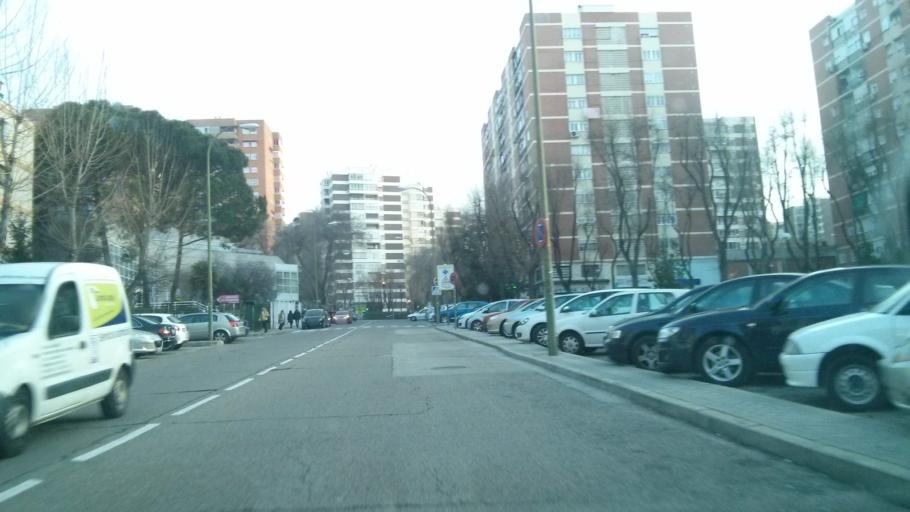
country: ES
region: Madrid
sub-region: Provincia de Madrid
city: Tetuan de las Victorias
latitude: 40.4787
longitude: -3.7024
